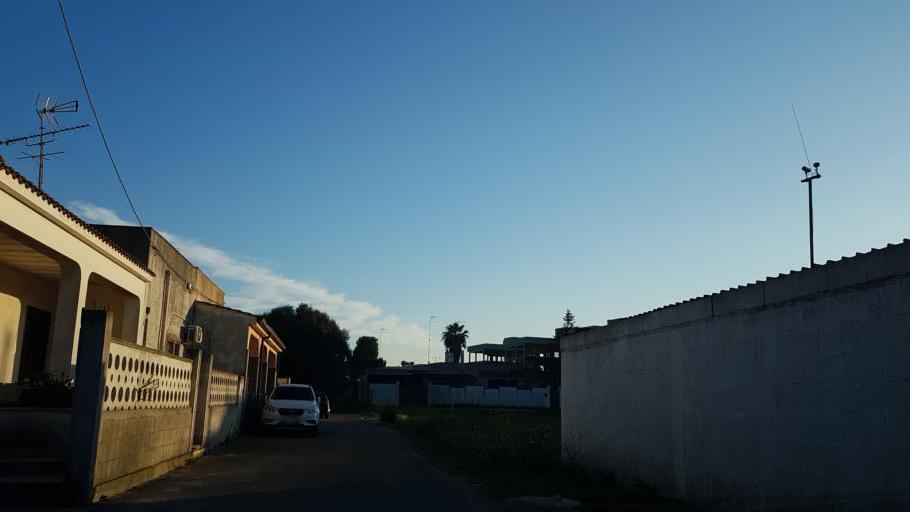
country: IT
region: Apulia
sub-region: Provincia di Brindisi
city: Tuturano
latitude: 40.5440
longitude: 17.9528
